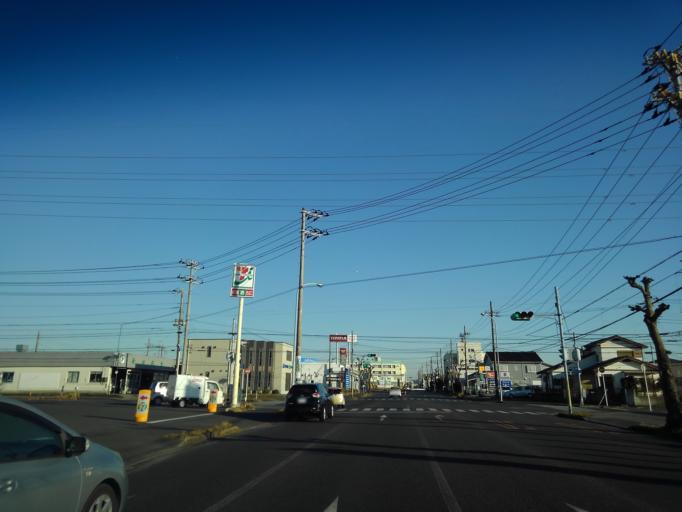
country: JP
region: Chiba
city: Kimitsu
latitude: 35.3184
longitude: 139.9196
